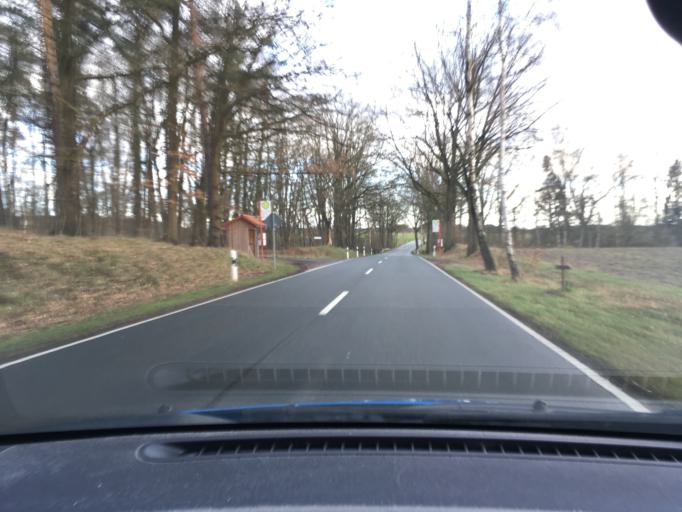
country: DE
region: Lower Saxony
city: Hanstedt
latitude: 53.2219
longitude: 10.0259
